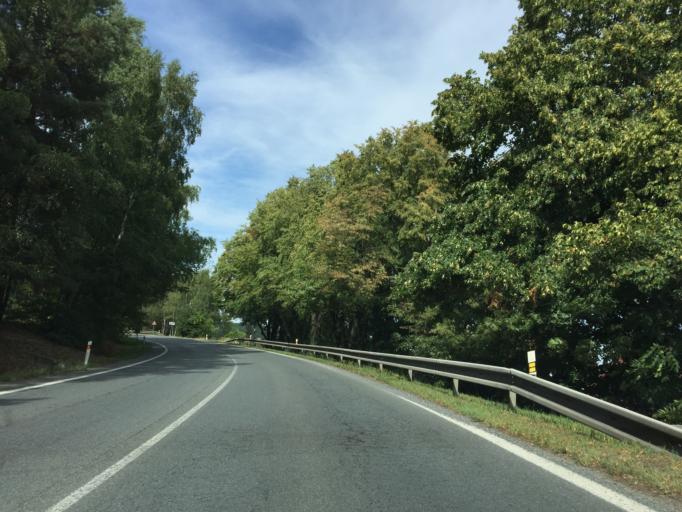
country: CZ
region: Central Bohemia
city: Votice
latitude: 49.5739
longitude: 14.6612
